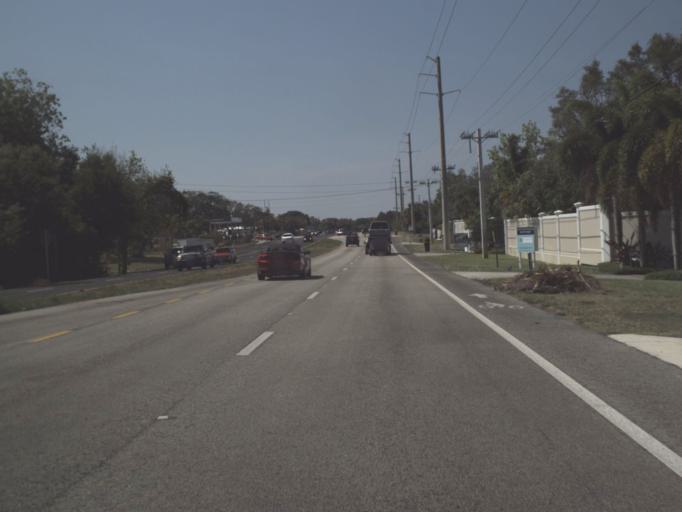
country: US
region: Florida
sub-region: Brevard County
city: South Patrick Shores
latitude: 28.2170
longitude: -80.6676
